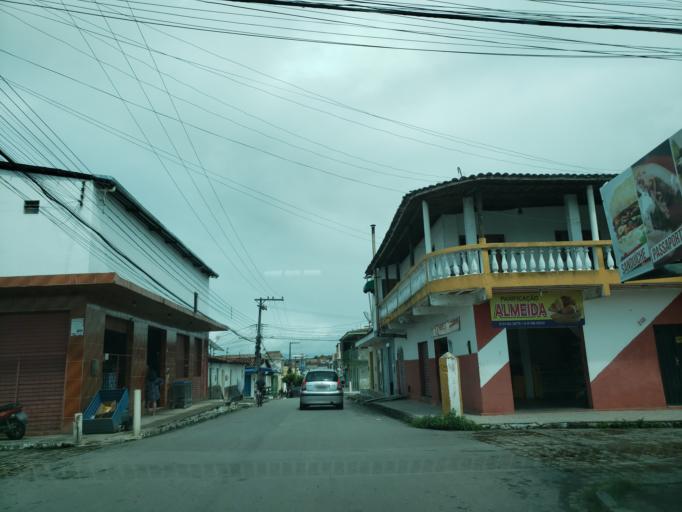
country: BR
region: Alagoas
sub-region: Uniao Dos Palmares
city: Uniao dos Palmares
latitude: -9.1585
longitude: -36.0259
